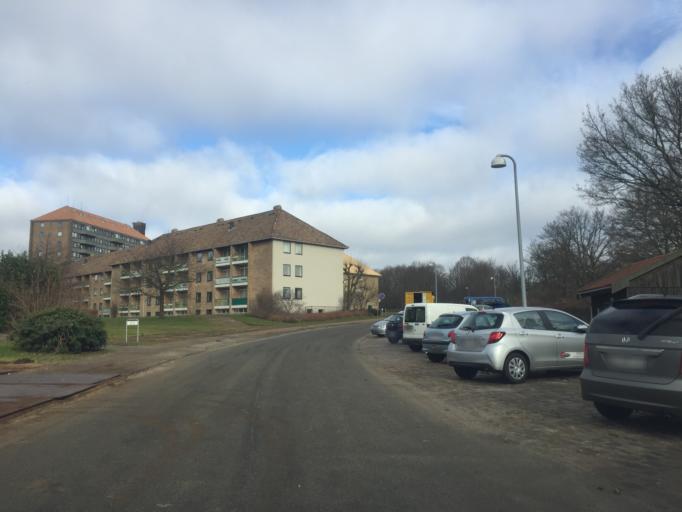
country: DK
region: Capital Region
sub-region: Lyngby-Tarbaek Kommune
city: Kongens Lyngby
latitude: 55.7787
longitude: 12.5162
